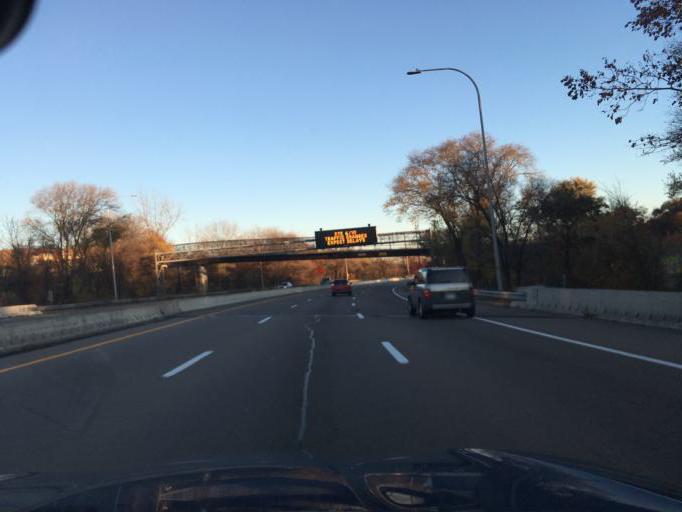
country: US
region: Rhode Island
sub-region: Providence County
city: North Providence
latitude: 41.8216
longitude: -71.4545
